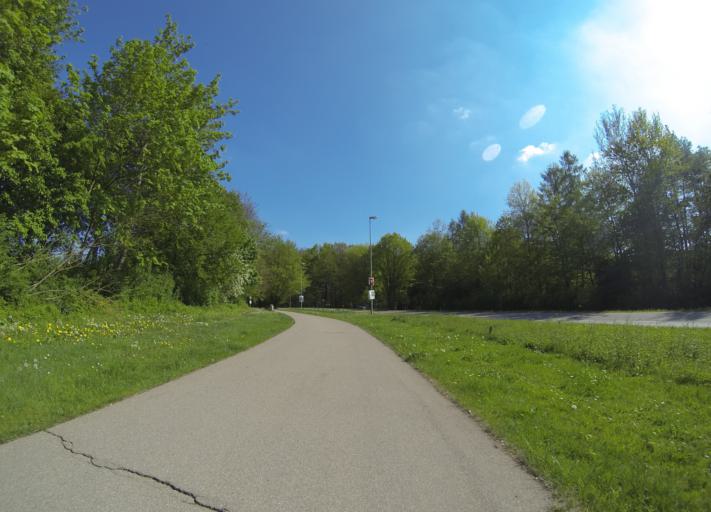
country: DE
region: Baden-Wuerttemberg
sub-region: Tuebingen Region
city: Staig
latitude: 48.3473
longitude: 9.9688
